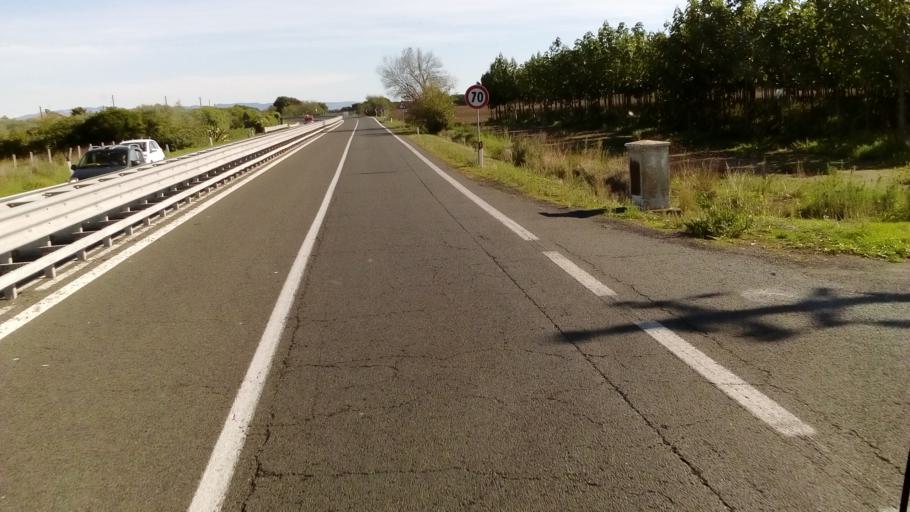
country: IT
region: Latium
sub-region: Provincia di Viterbo
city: Montalto di Castro
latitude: 42.3285
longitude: 11.6316
